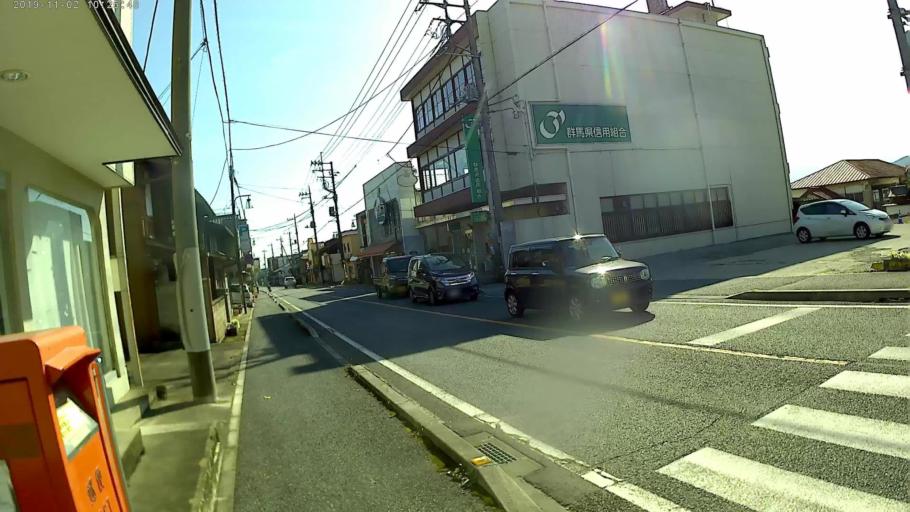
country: JP
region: Gunma
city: Annaka
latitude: 36.3132
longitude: 138.8015
